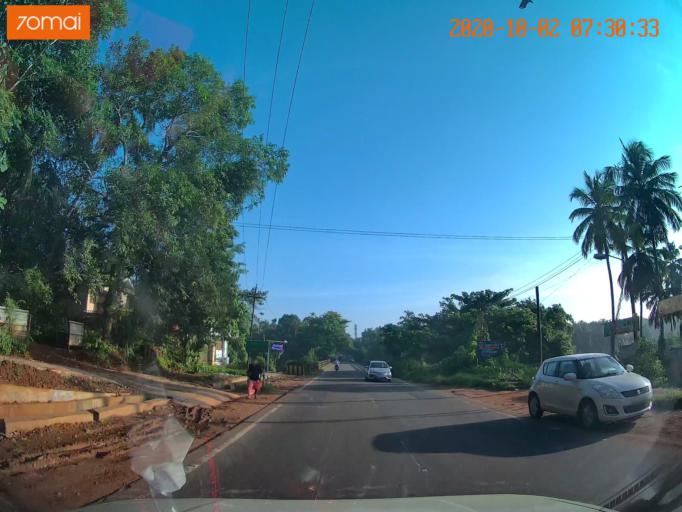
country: IN
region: Kerala
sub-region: Malappuram
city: Pariyapuram
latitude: 11.0425
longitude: 75.9395
